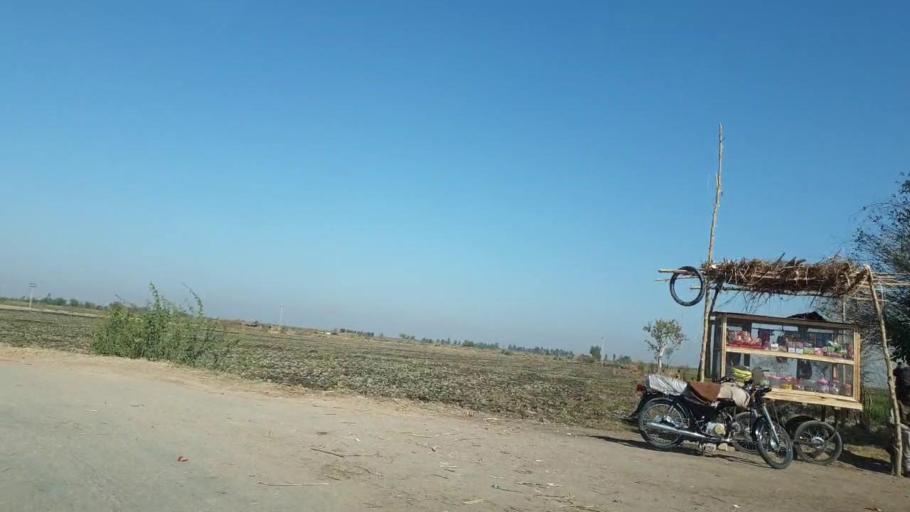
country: PK
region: Sindh
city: Mirpur Khas
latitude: 25.6038
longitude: 69.0449
